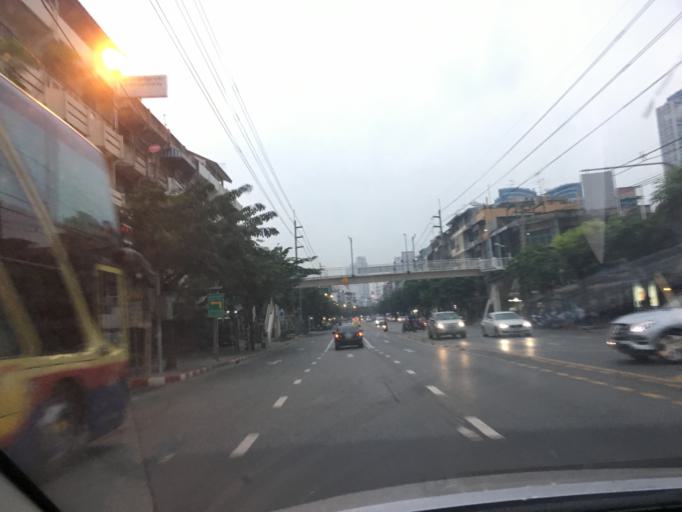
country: TH
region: Bangkok
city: Bang Kho Laem
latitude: 13.7095
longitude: 100.4960
